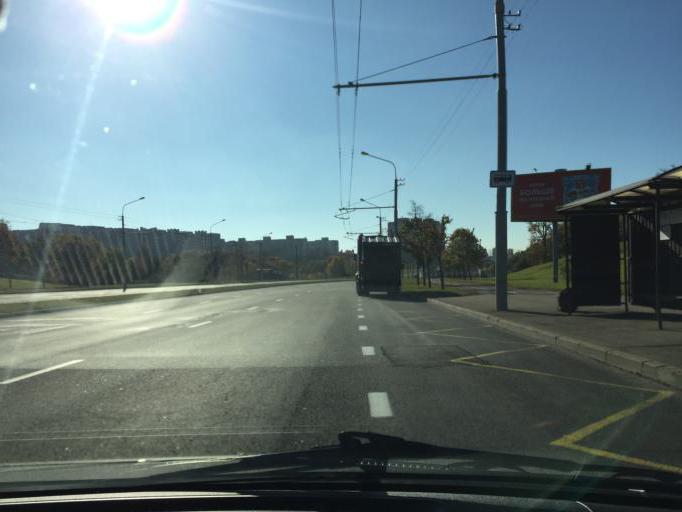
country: BY
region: Minsk
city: Syenitsa
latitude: 53.8574
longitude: 27.5387
